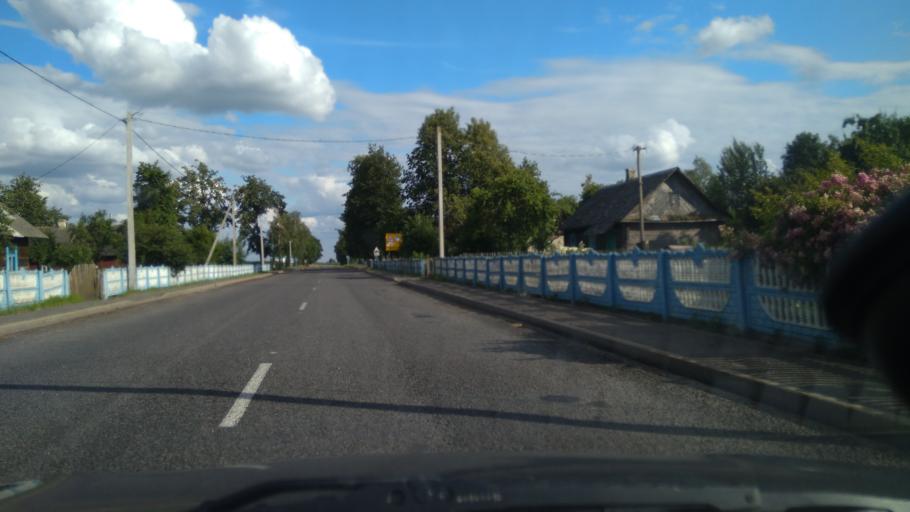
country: BY
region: Grodnenskaya
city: Masty
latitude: 53.3218
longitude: 24.6852
